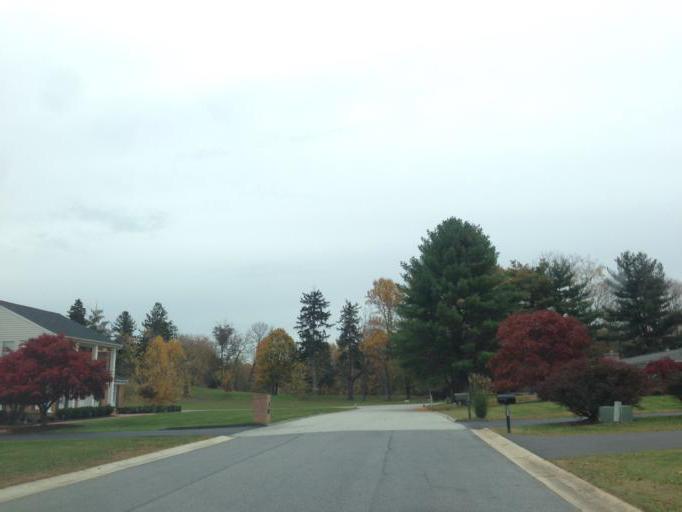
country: US
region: Maryland
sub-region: Howard County
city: Ellicott City
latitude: 39.3058
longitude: -76.8269
